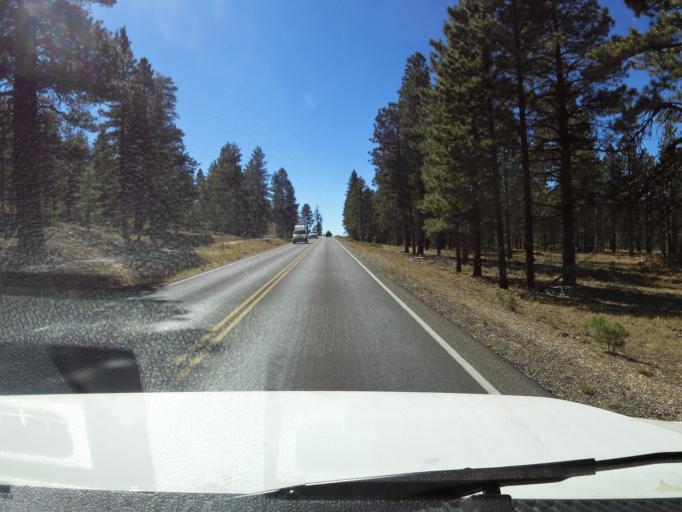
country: US
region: Utah
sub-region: Garfield County
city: Panguitch
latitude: 37.6209
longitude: -112.1731
